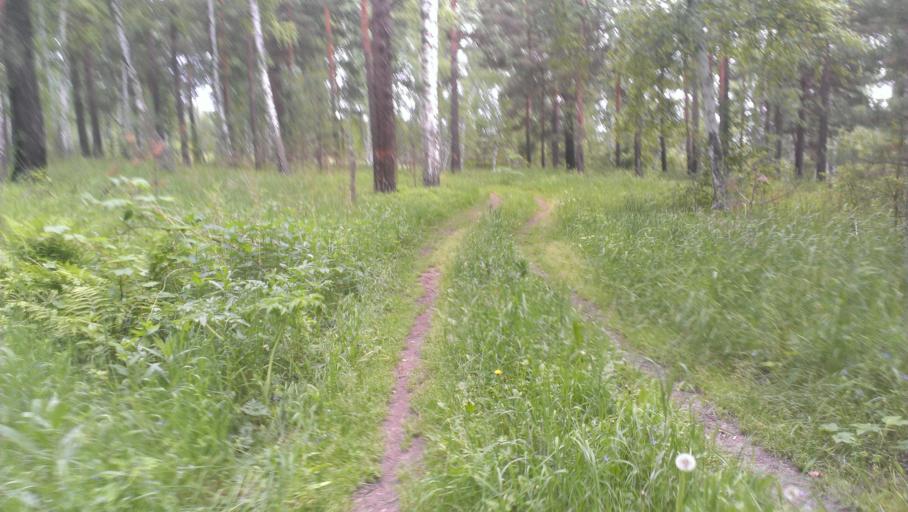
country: RU
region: Altai Krai
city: Sannikovo
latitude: 53.3385
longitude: 84.0504
